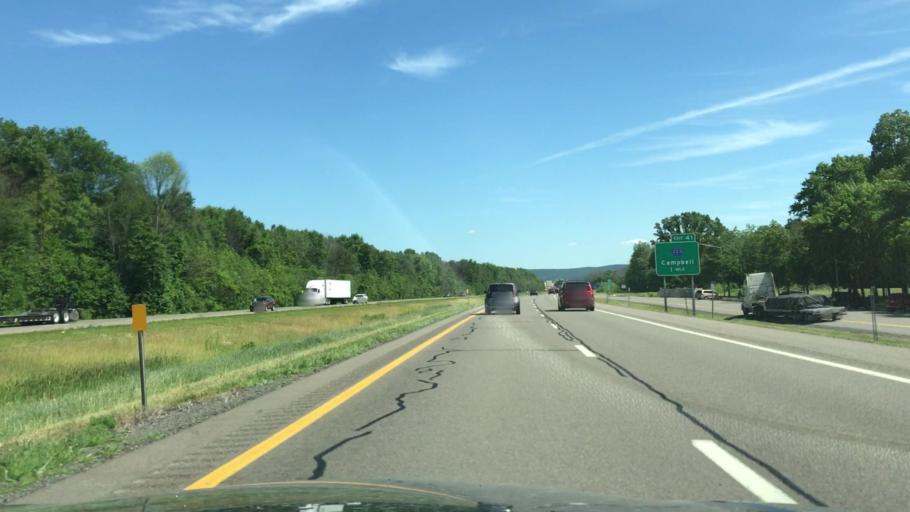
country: US
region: New York
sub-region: Steuben County
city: Gang Mills
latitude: 42.2440
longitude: -77.1985
